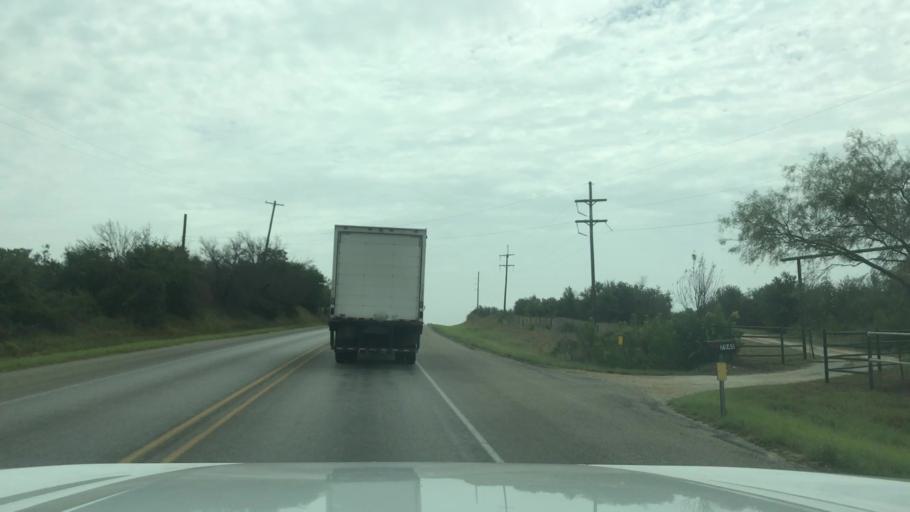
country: US
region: Texas
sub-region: Erath County
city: Dublin
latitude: 32.0904
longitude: -98.4395
